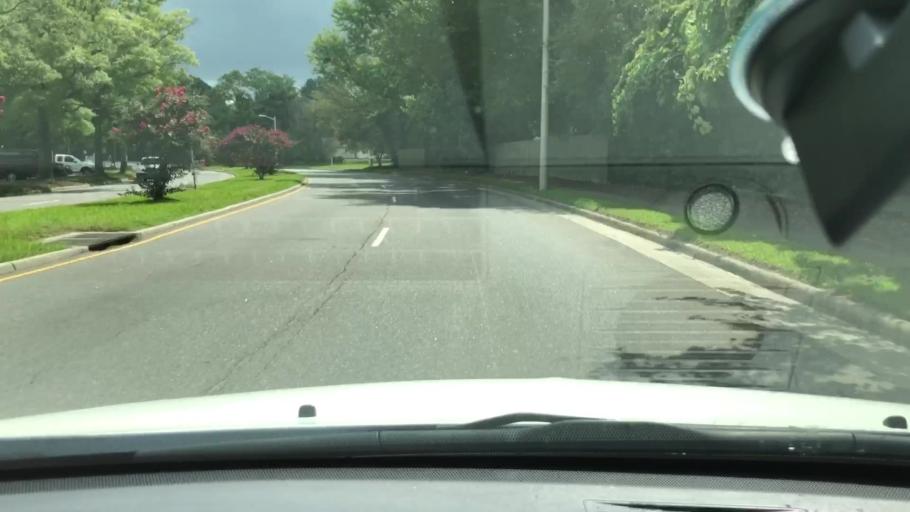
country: US
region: Virginia
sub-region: City of Chesapeake
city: Chesapeake
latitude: 36.8102
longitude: -76.2120
